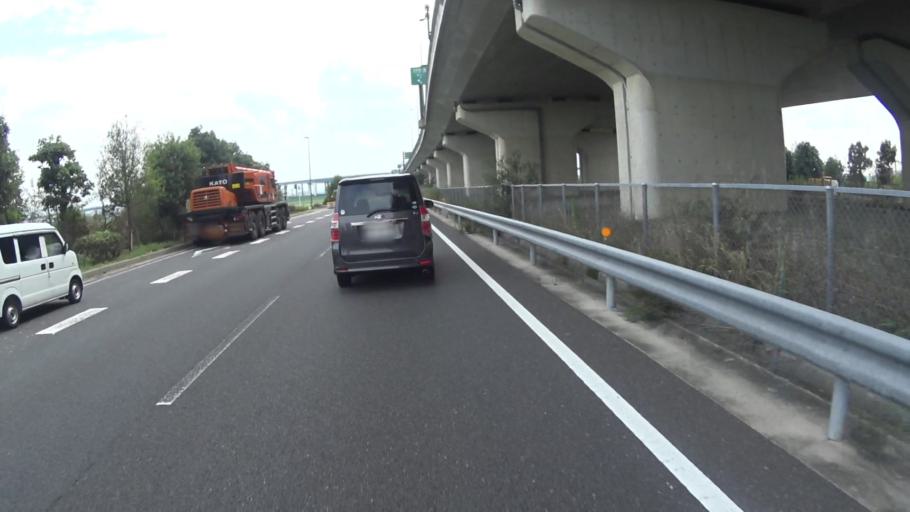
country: JP
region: Kyoto
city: Uji
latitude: 34.9060
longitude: 135.7499
